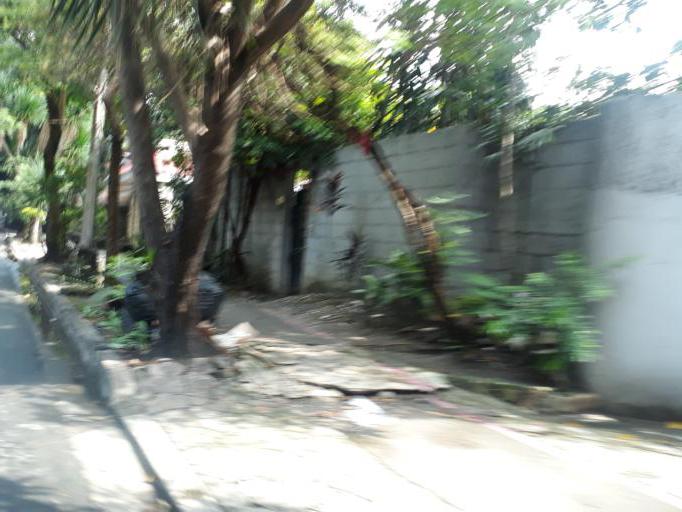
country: PH
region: Metro Manila
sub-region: San Juan
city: San Juan
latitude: 14.6207
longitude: 121.0276
